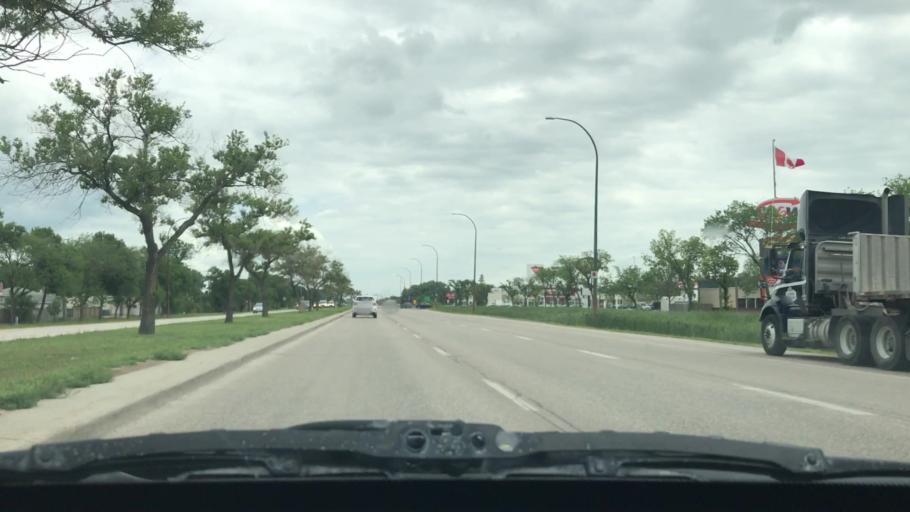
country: CA
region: Manitoba
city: Winnipeg
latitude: 49.8560
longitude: -97.0721
